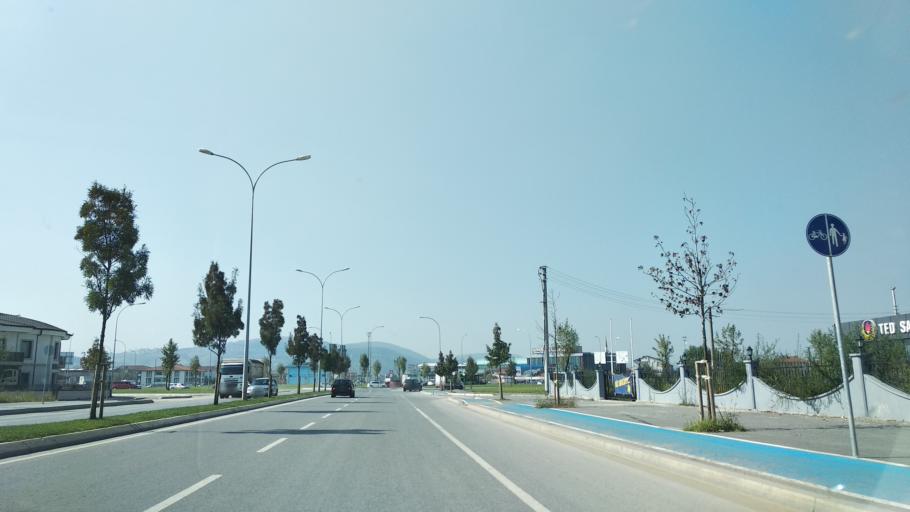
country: TR
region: Sakarya
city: Adapazari
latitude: 40.7886
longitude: 30.3759
